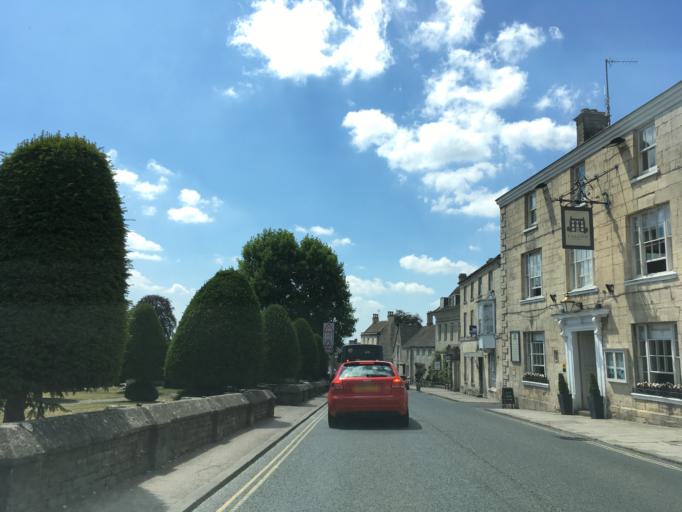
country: GB
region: England
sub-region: Gloucestershire
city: Painswick
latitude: 51.7859
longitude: -2.1953
